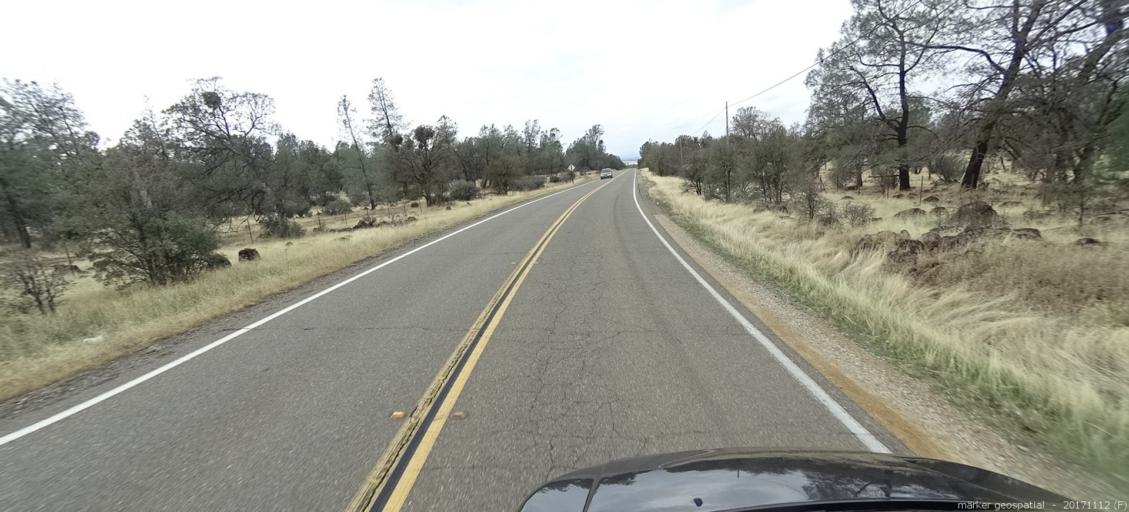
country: US
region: California
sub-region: Shasta County
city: Palo Cedro
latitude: 40.4811
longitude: -122.0838
